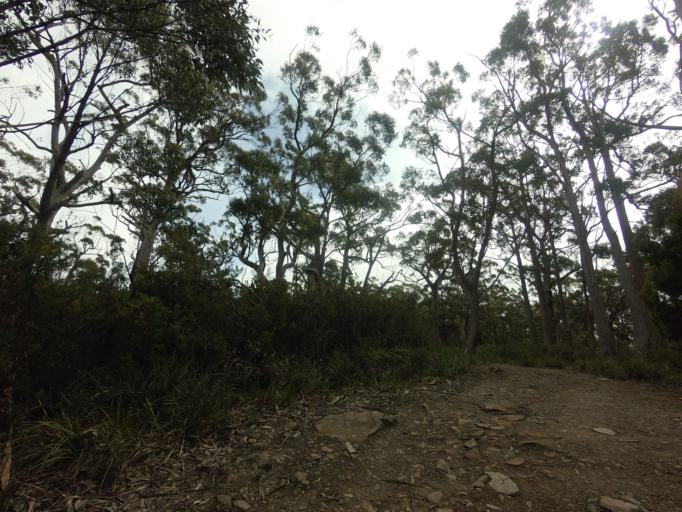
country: AU
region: Tasmania
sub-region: Huon Valley
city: Geeveston
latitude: -43.4684
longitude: 146.9316
